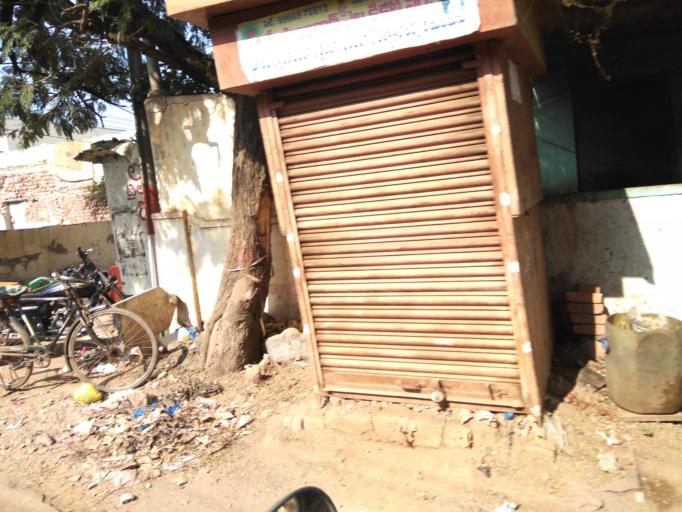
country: IN
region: Andhra Pradesh
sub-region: Nellore
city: Nellore
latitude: 14.4443
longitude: 79.9855
